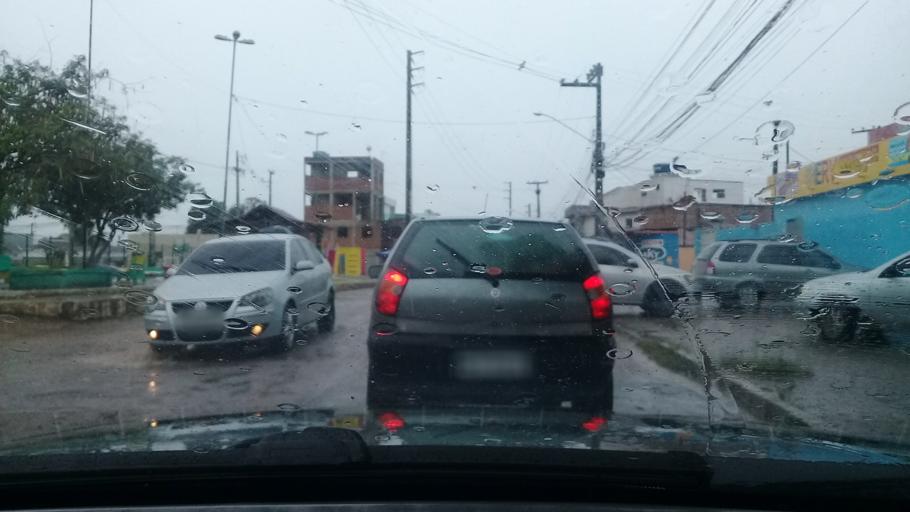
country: BR
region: Pernambuco
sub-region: Paulista
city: Paulista
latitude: -7.9535
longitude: -34.8897
